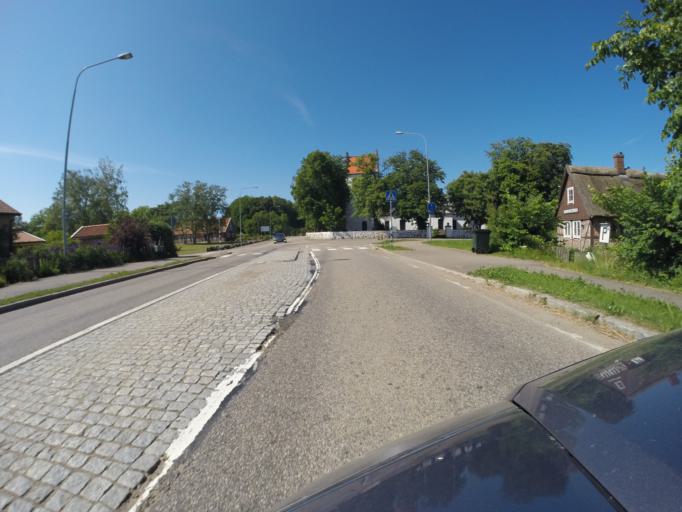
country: SE
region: Skane
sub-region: Helsingborg
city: Odakra
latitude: 56.1081
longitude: 12.6920
